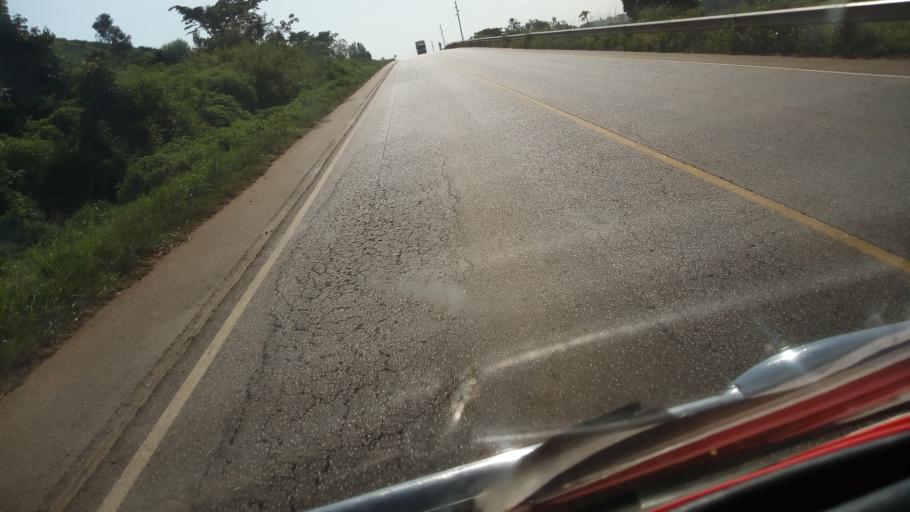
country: UG
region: Eastern Region
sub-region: Bugiri District
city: Bugiri
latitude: 0.5284
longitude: 33.8557
